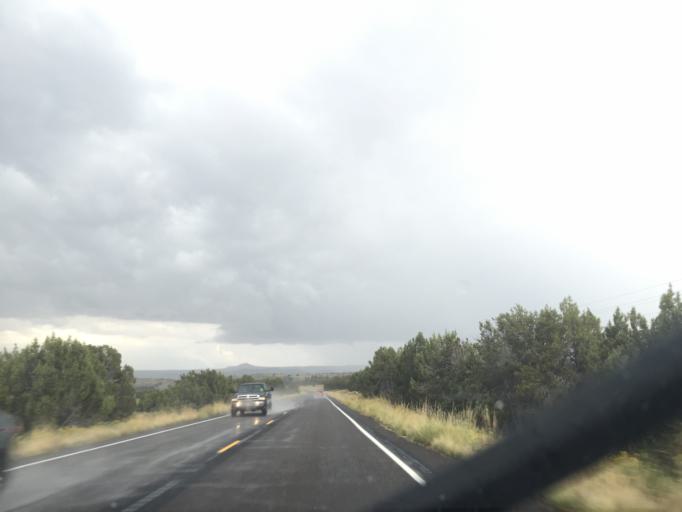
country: US
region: Utah
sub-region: Kane County
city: Kanab
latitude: 37.2431
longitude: -112.7528
